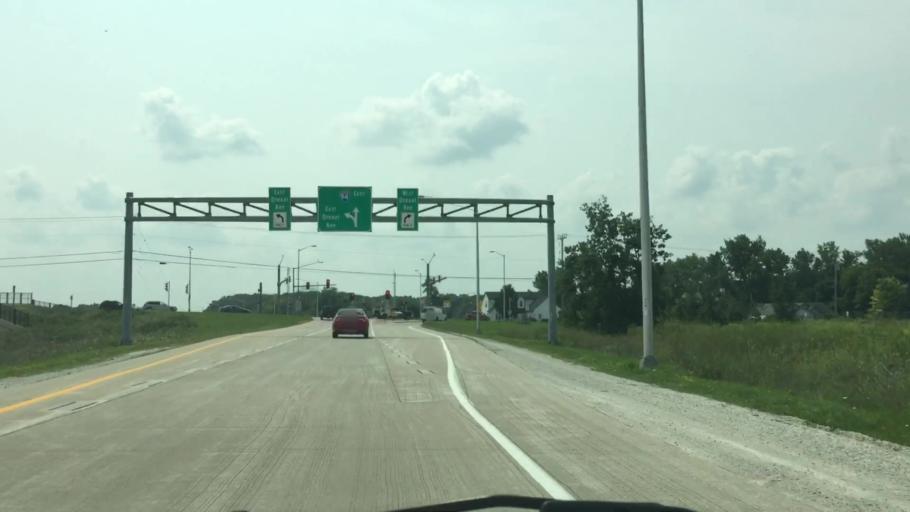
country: US
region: Wisconsin
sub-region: Milwaukee County
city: Greendale
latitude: 42.9030
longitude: -87.9369
